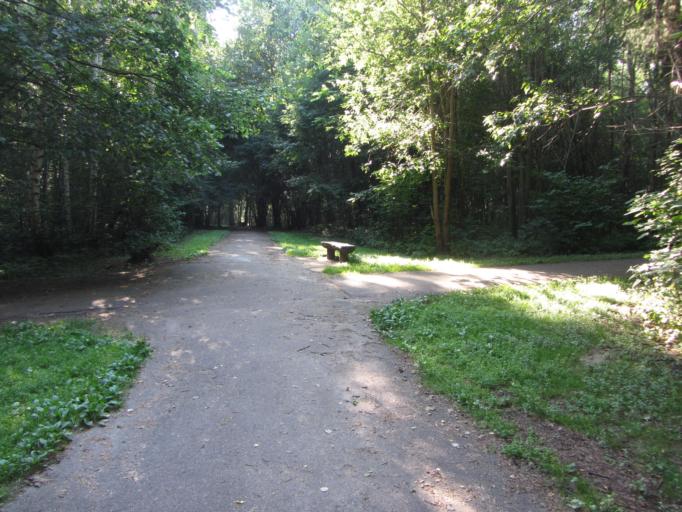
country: LT
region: Vilnius County
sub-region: Vilnius
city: Fabijoniskes
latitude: 54.7321
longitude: 25.2694
